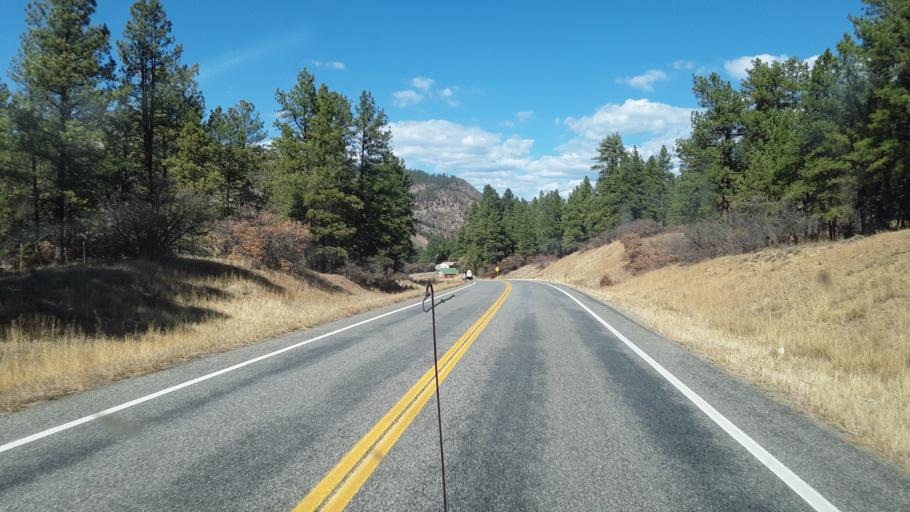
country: US
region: Colorado
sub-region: La Plata County
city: Bayfield
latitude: 37.2207
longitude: -107.3395
